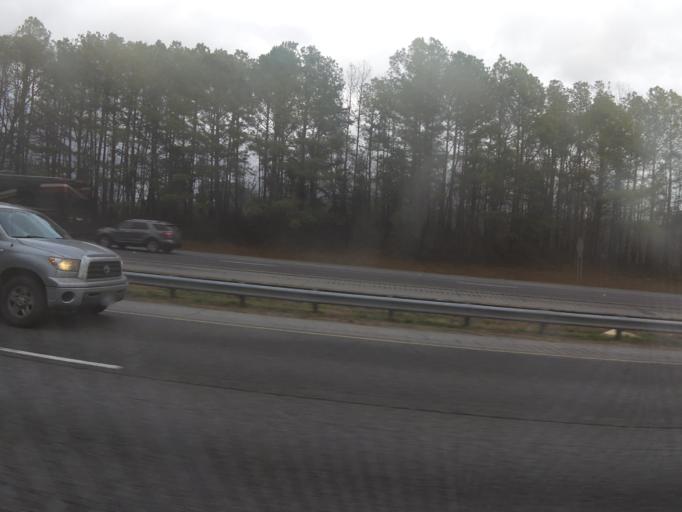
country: US
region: Georgia
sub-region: Gordon County
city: Calhoun
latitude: 34.6246
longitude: -84.9701
